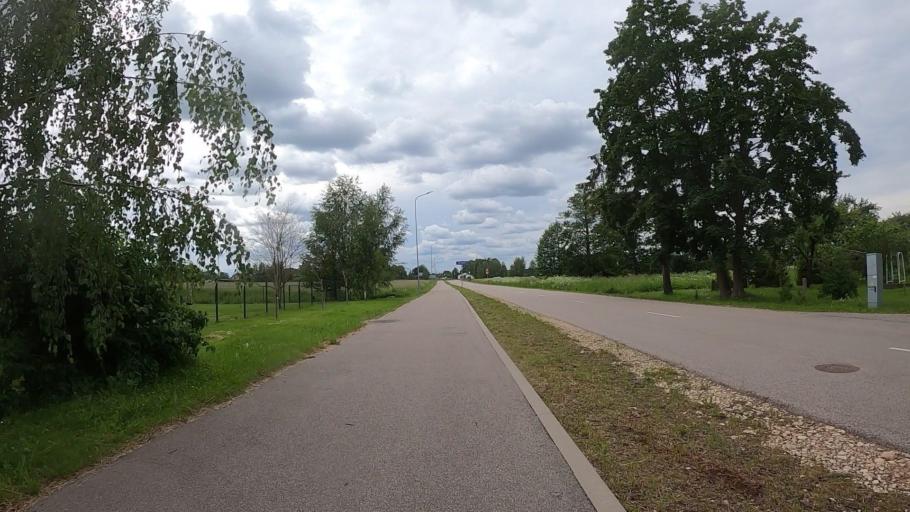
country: LV
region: Marupe
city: Marupe
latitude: 56.8778
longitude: 23.9751
